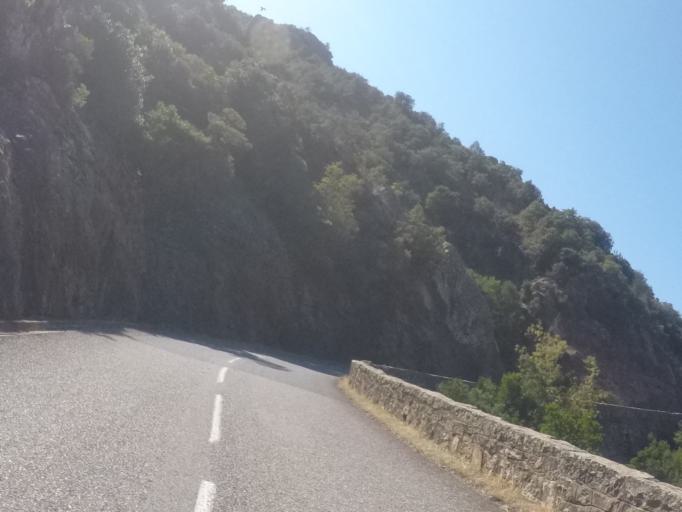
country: FR
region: Corsica
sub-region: Departement de la Haute-Corse
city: Calvi
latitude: 42.3683
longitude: 8.6707
